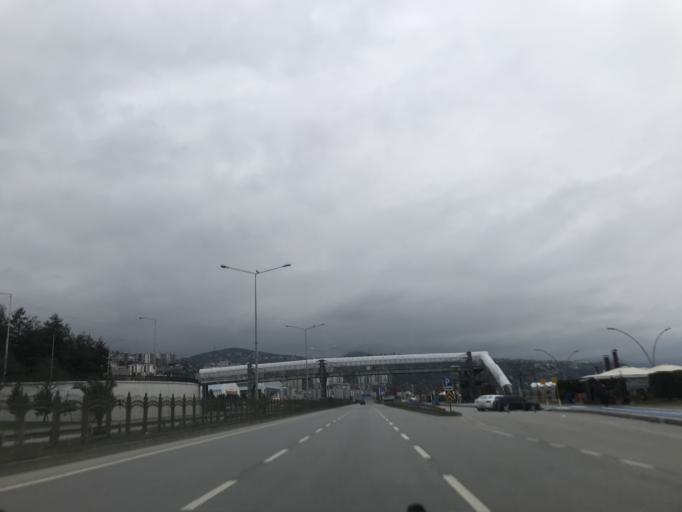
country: TR
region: Trabzon
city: Trabzon
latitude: 40.9987
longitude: 39.6765
